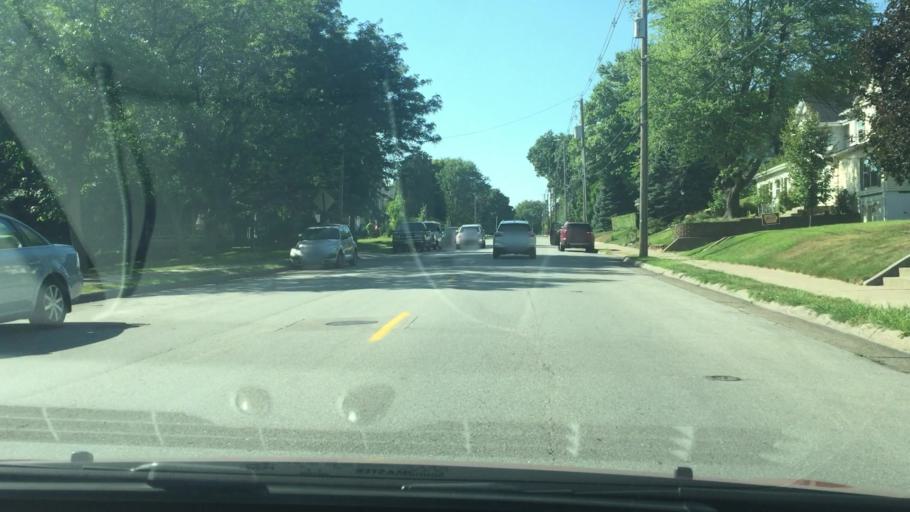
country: US
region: Iowa
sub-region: Muscatine County
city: Muscatine
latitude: 41.4361
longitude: -91.0548
